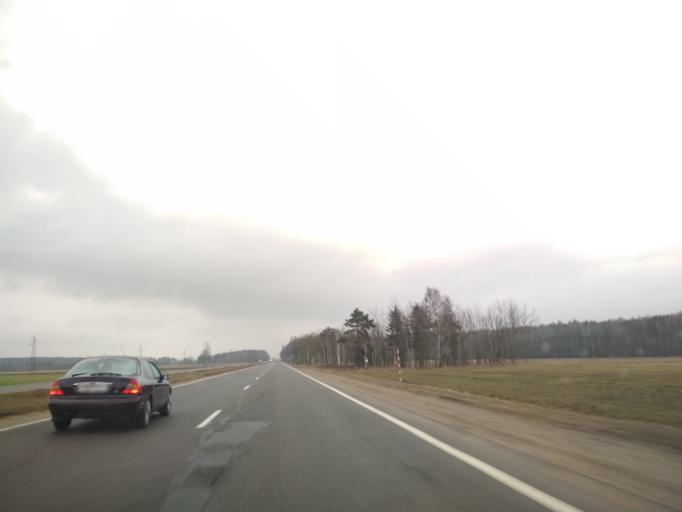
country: BY
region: Minsk
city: Dukora
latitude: 53.6308
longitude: 28.0219
